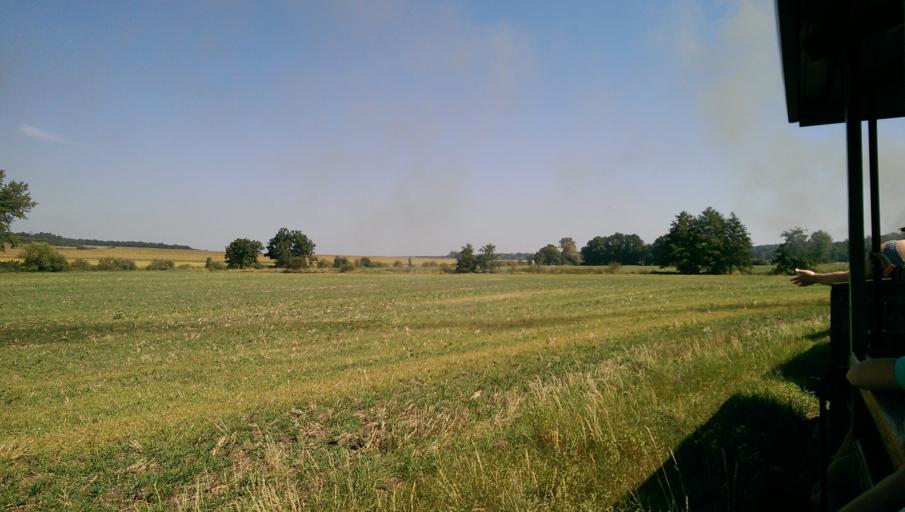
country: CZ
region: Central Bohemia
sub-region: Okres Kolin
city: Kolin
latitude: 50.0536
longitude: 15.2507
